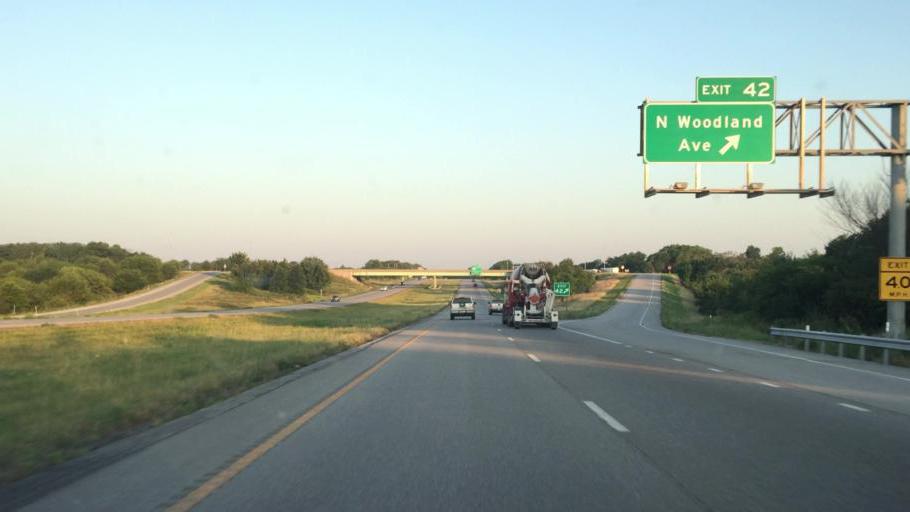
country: US
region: Missouri
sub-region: Clay County
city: Smithville
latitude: 39.3114
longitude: -94.5520
